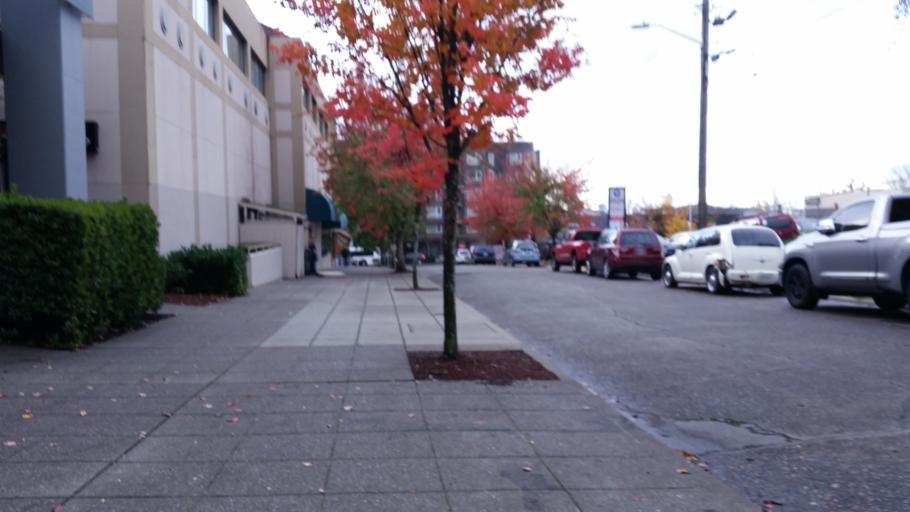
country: US
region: Washington
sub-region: King County
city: Seattle
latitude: 47.6622
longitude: -122.3184
